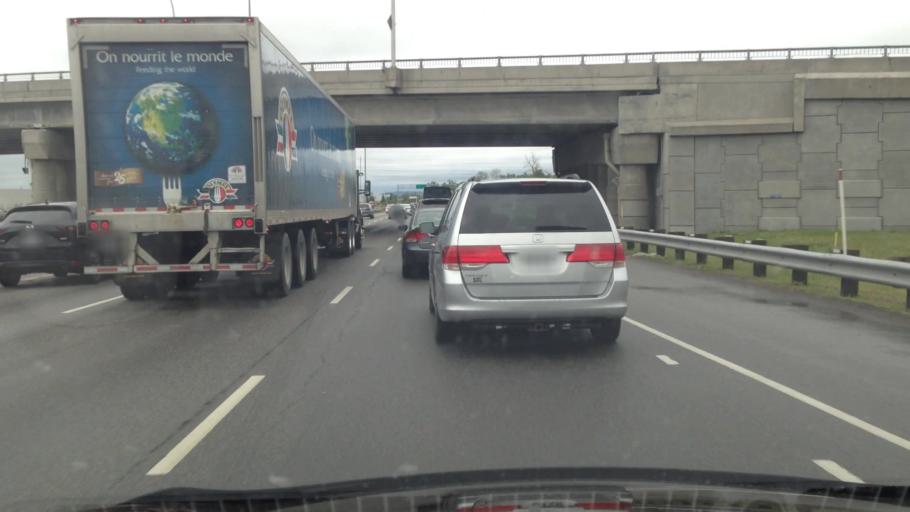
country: CA
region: Quebec
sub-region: Laurentides
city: Rosemere
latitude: 45.5822
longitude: -73.7799
